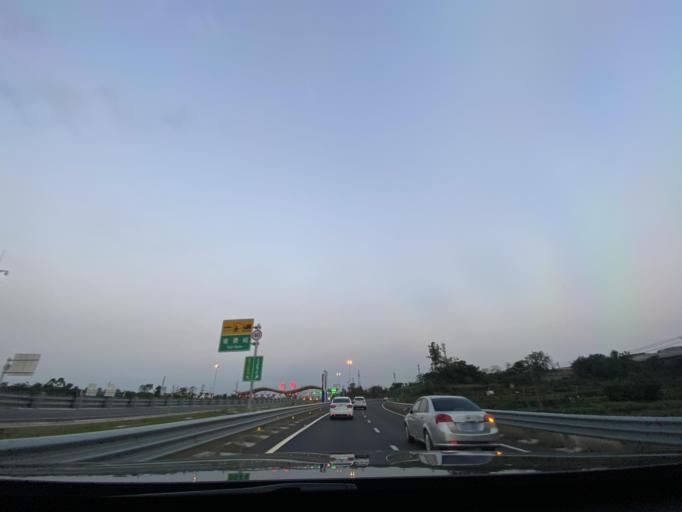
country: CN
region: Sichuan
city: Chengdu
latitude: 30.5671
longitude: 104.1412
